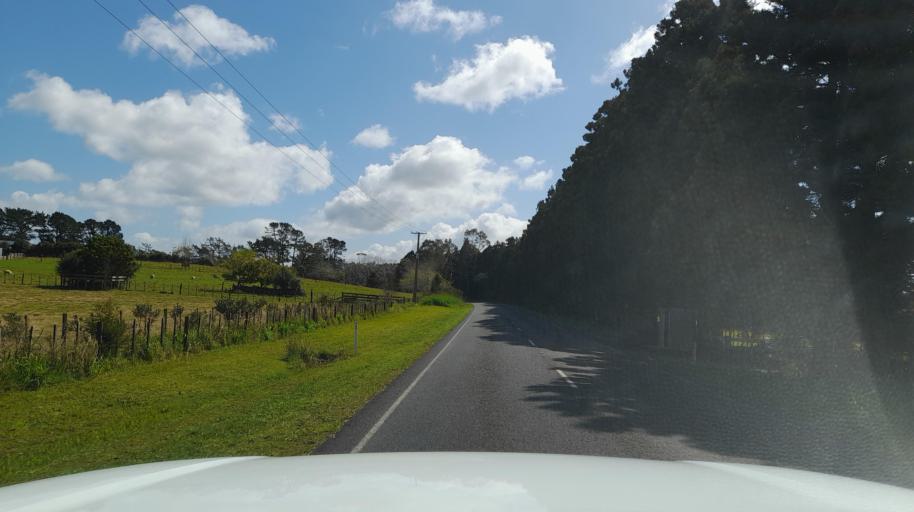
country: NZ
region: Northland
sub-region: Far North District
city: Kerikeri
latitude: -35.2401
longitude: 173.8842
